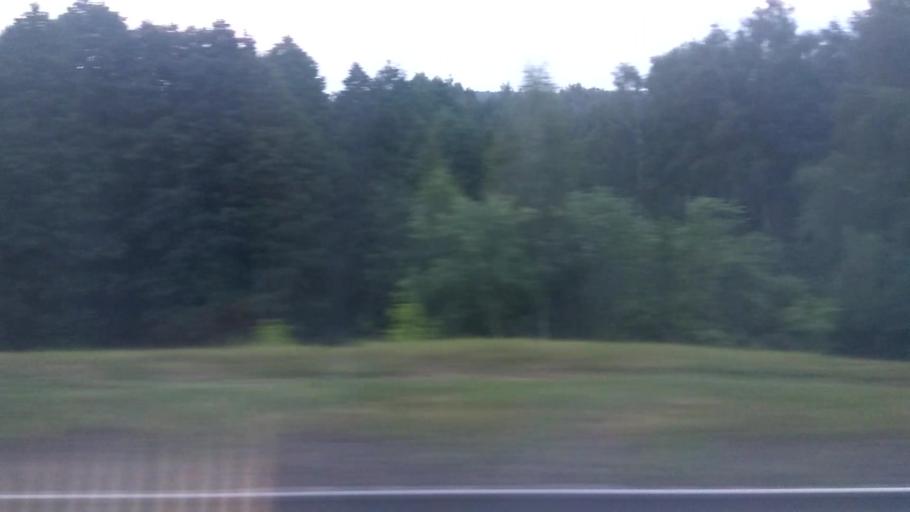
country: RU
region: Moscow
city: Zagor'ye
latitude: 55.5686
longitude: 37.6657
